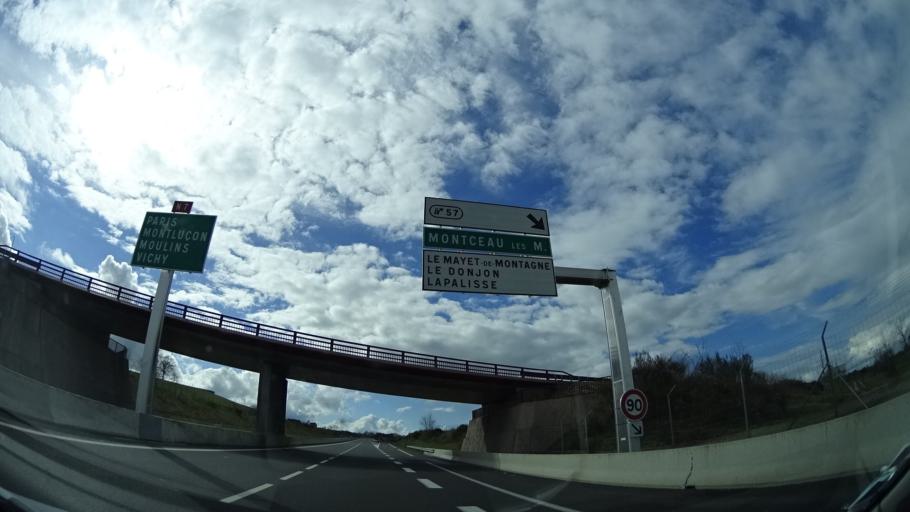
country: FR
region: Auvergne
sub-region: Departement de l'Allier
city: Lapalisse
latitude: 46.2195
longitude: 3.6828
